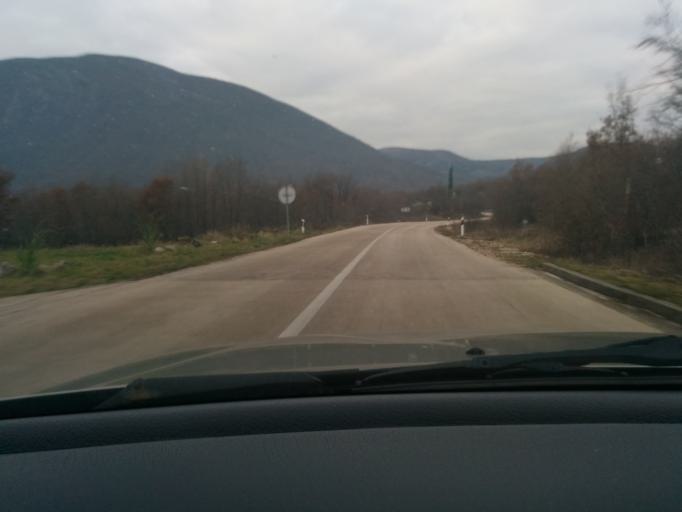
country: HR
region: Splitsko-Dalmatinska
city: Sinj
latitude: 43.7061
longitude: 16.5995
